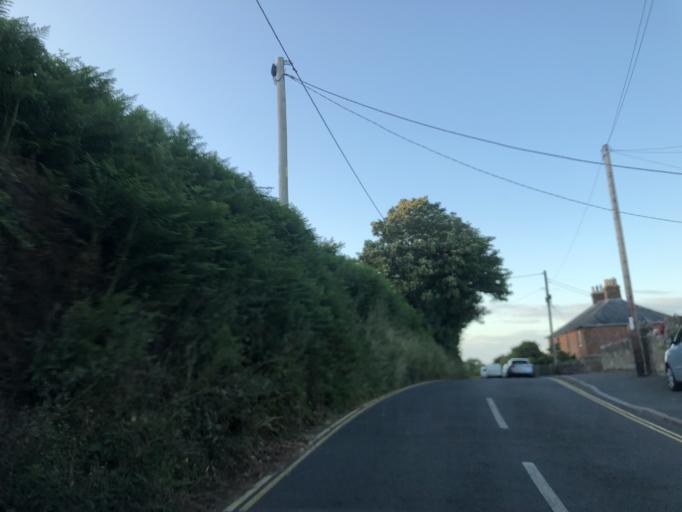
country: GB
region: England
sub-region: Isle of Wight
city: Niton
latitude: 50.5912
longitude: -1.2836
